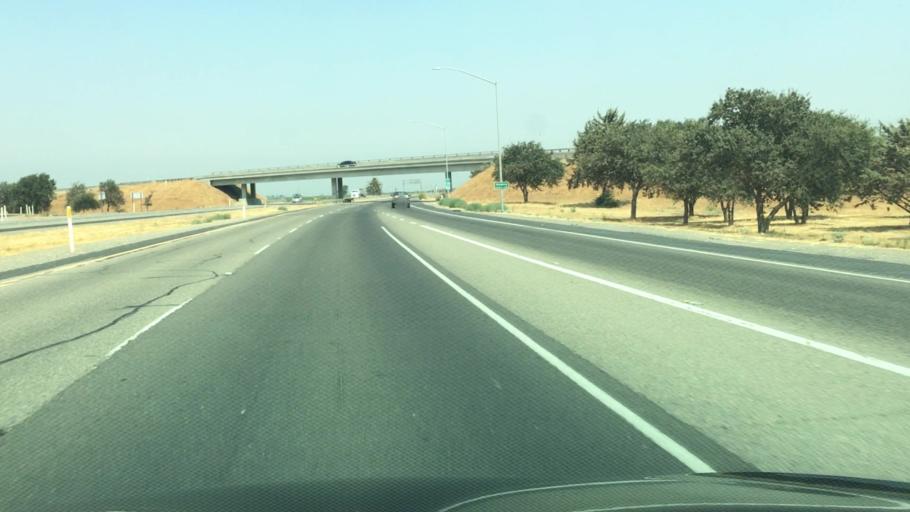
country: US
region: California
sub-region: Merced County
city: Dos Palos
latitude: 37.0827
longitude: -120.4946
